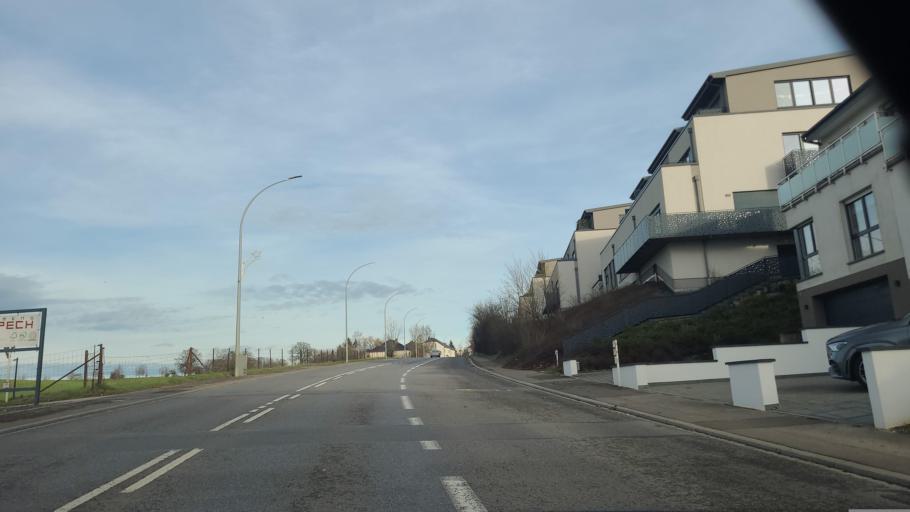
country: LU
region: Luxembourg
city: Schouweiler
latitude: 49.5839
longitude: 5.9631
